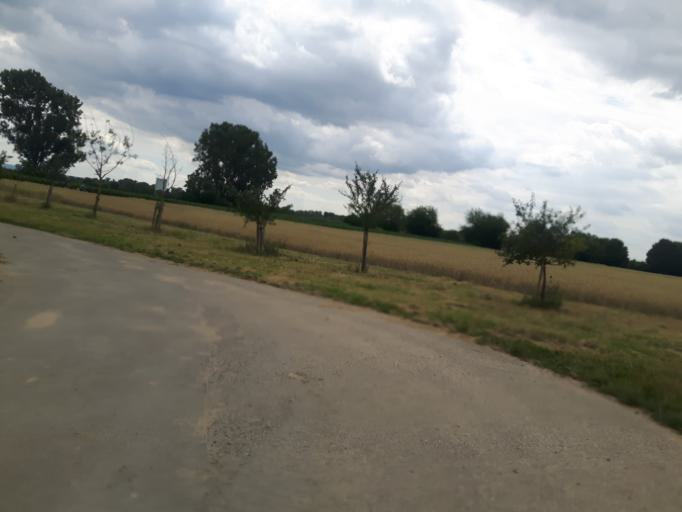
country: DE
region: Rheinland-Pfalz
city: Waldsee
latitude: 49.3861
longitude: 8.4453
